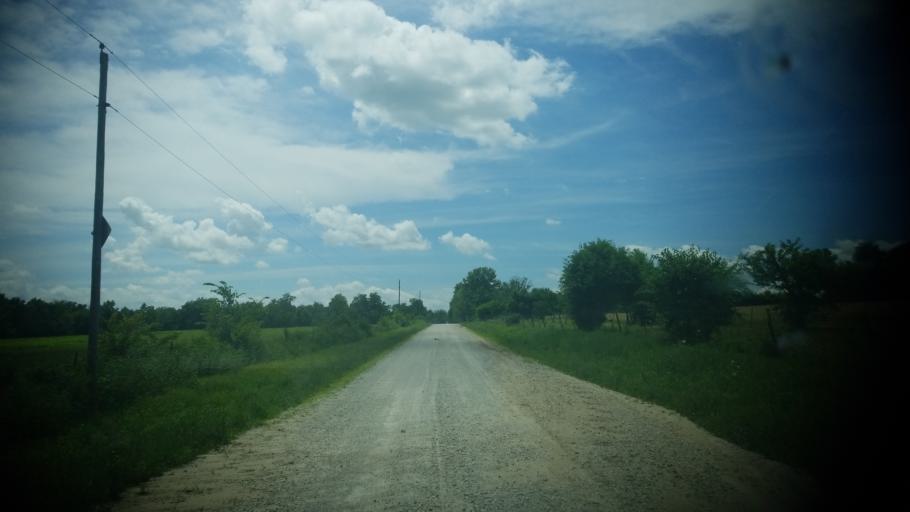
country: US
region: Missouri
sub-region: Pike County
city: Bowling Green
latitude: 39.3088
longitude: -91.3245
